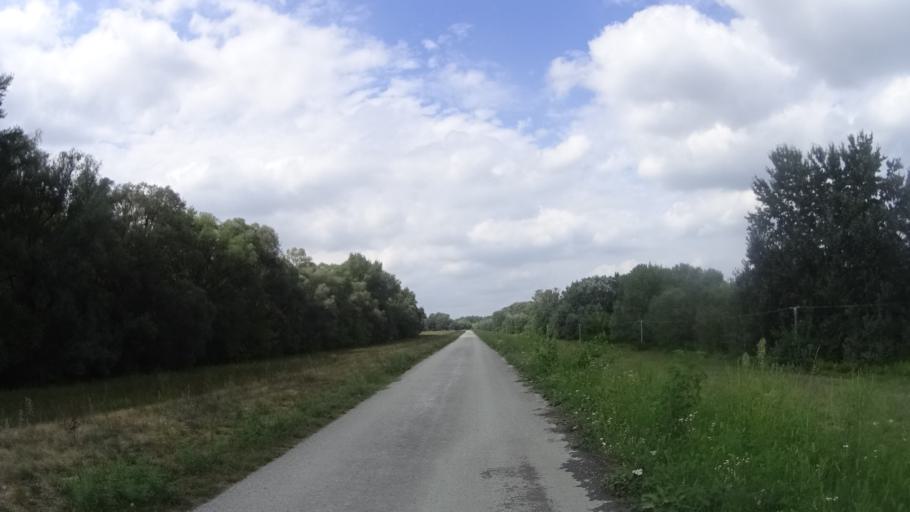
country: SK
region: Trnavsky
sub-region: Okres Dunajska Streda
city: Velky Meder
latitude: 47.7860
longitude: 17.6940
